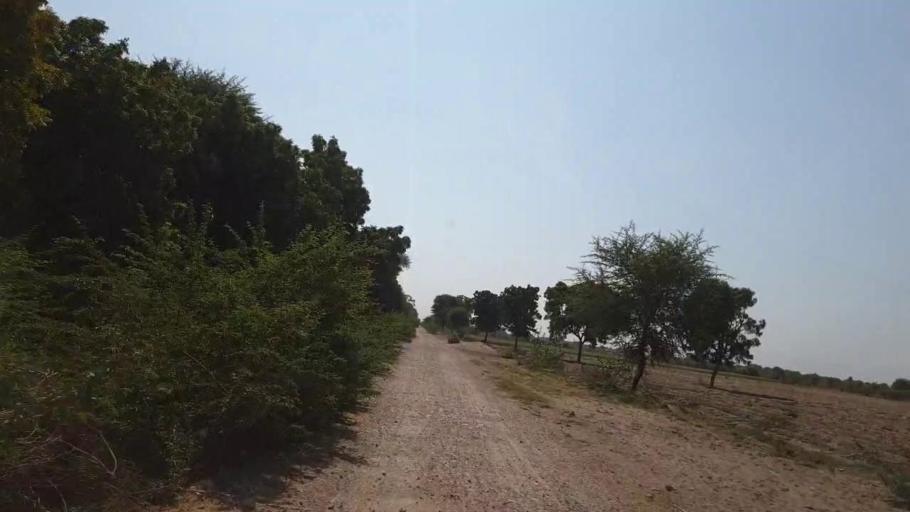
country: PK
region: Sindh
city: Nabisar
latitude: 25.0730
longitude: 69.5414
